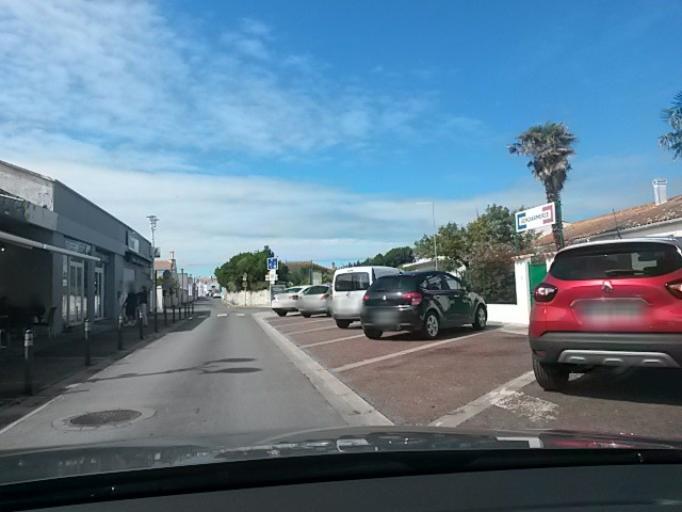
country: FR
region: Poitou-Charentes
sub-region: Departement de la Charente-Maritime
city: Dolus-d'Oleron
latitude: 45.9175
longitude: -1.3313
